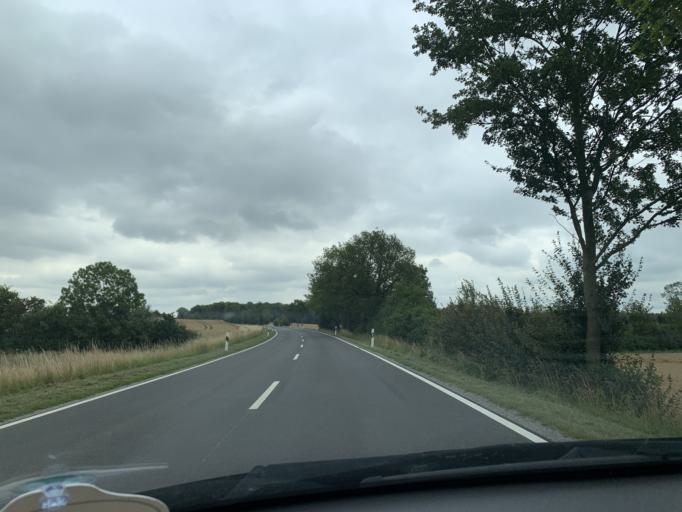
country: DE
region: North Rhine-Westphalia
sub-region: Regierungsbezirk Munster
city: Wadersloh
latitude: 51.7586
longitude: 8.1857
